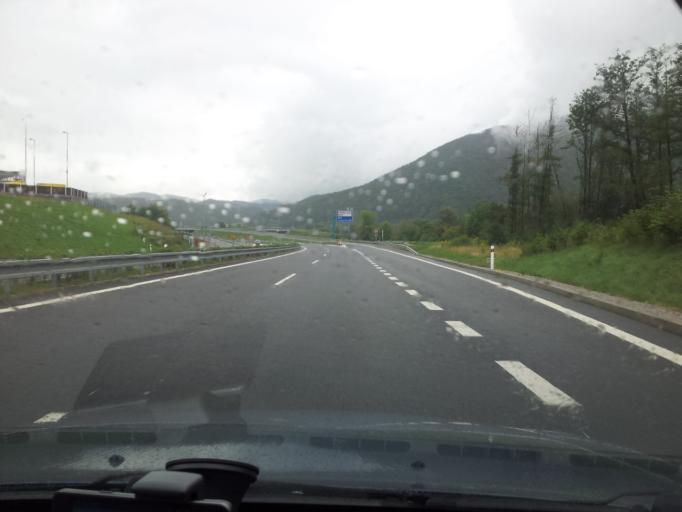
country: SK
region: Banskobystricky
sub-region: Okres Banska Bystrica
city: Banska Bystrica
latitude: 48.7416
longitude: 19.1815
